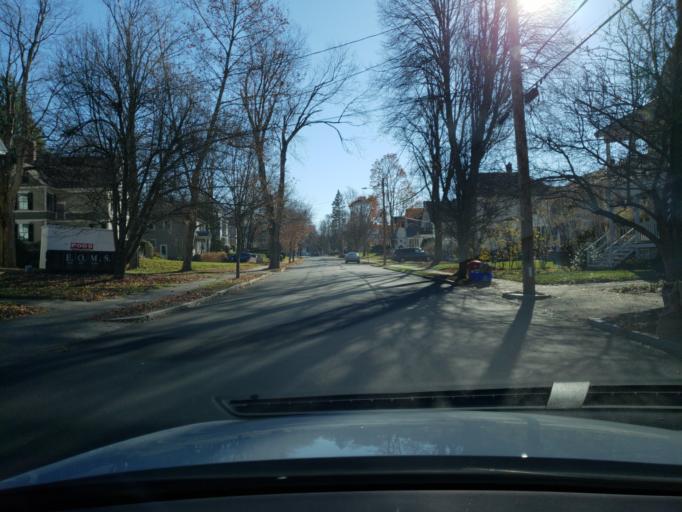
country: US
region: Massachusetts
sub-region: Essex County
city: Andover
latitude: 42.6614
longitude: -71.1401
